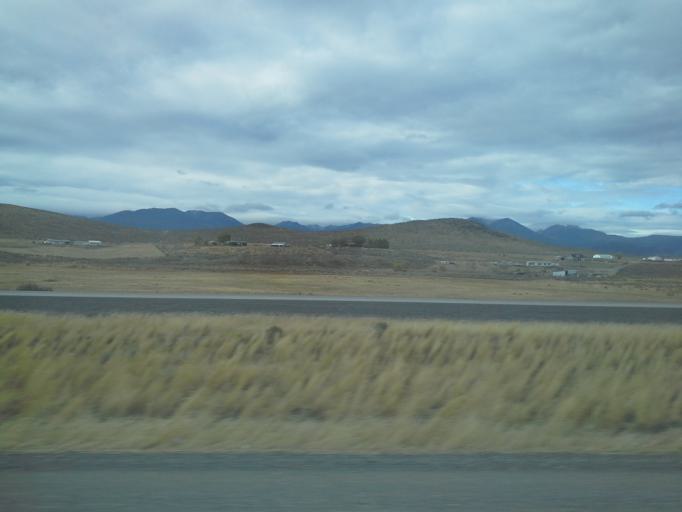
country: US
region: Oregon
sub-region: Baker County
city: Baker City
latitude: 44.9850
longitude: -117.8929
